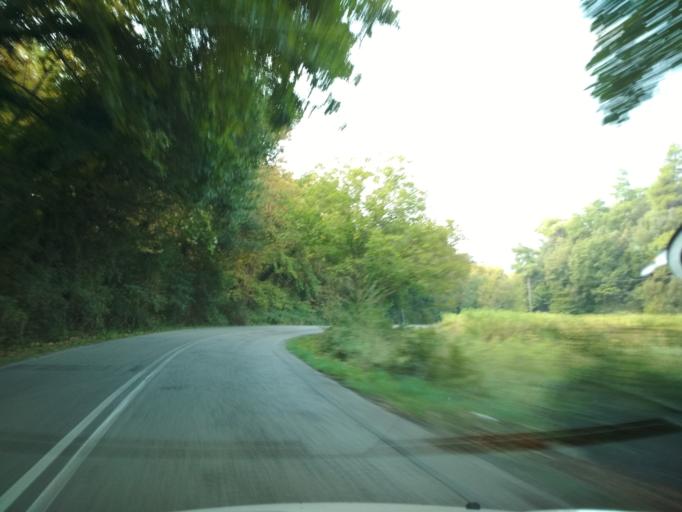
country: GR
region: Central Greece
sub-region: Nomos Evvoias
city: Prokopion
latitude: 38.7545
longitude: 23.4837
